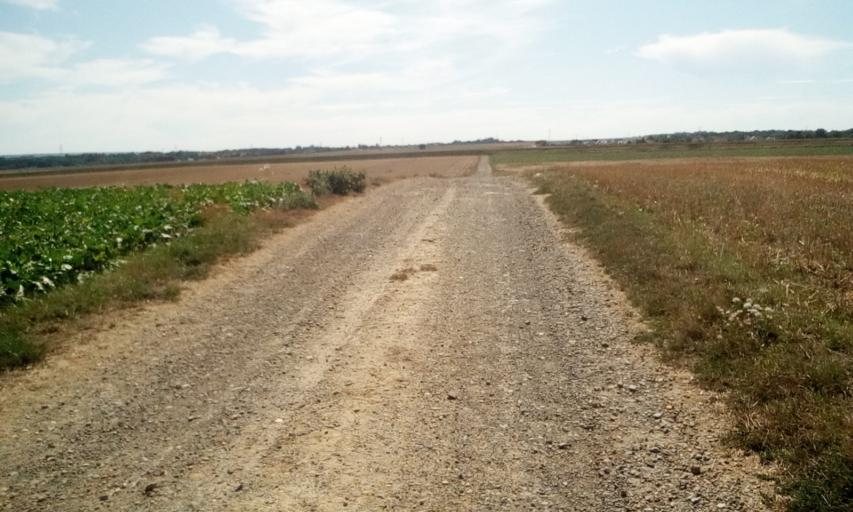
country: FR
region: Lower Normandy
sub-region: Departement du Calvados
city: Louvigny
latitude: 49.1511
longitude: -0.4090
